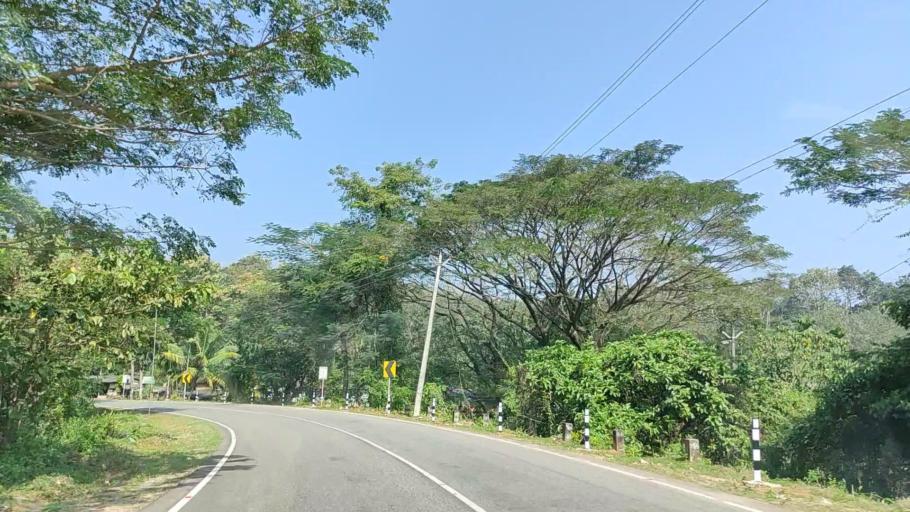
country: IN
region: Kerala
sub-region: Kollam
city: Punalur
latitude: 8.9279
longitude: 77.0642
